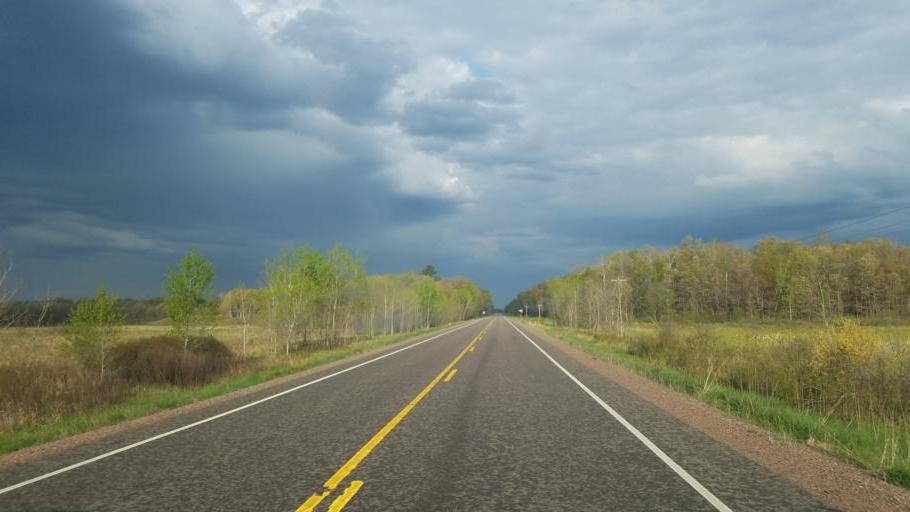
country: US
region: Wisconsin
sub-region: Wood County
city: Nekoosa
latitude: 44.3802
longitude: -90.1420
